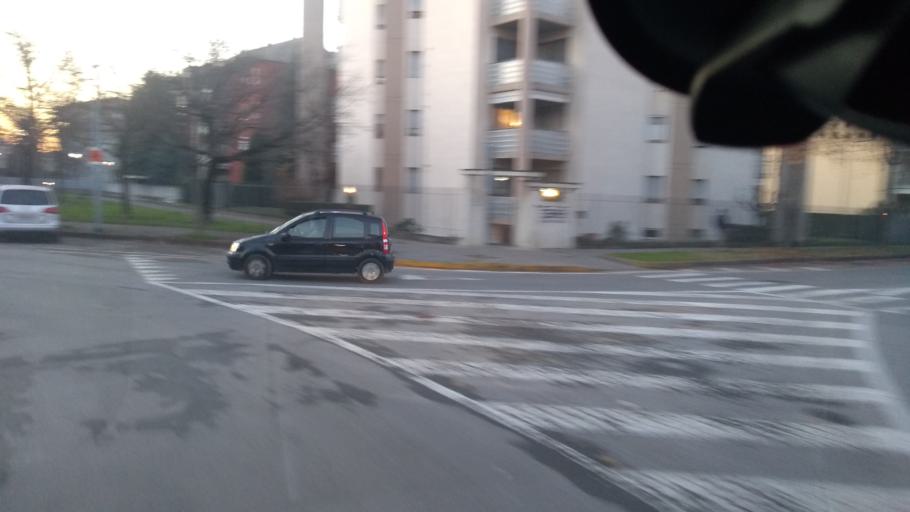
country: IT
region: Lombardy
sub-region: Provincia di Bergamo
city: Treviglio
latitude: 45.5195
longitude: 9.6005
